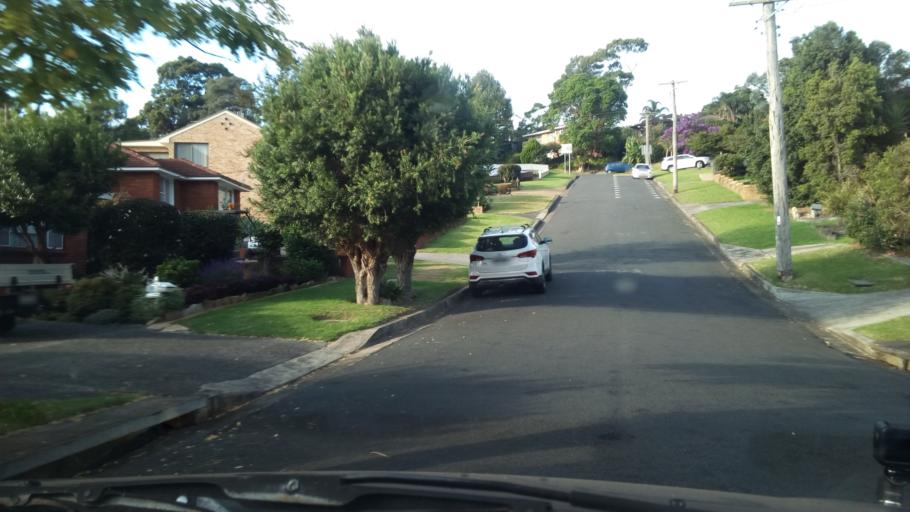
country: AU
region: New South Wales
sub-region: Wollongong
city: Mount Ousley
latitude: -34.3884
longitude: 150.8722
